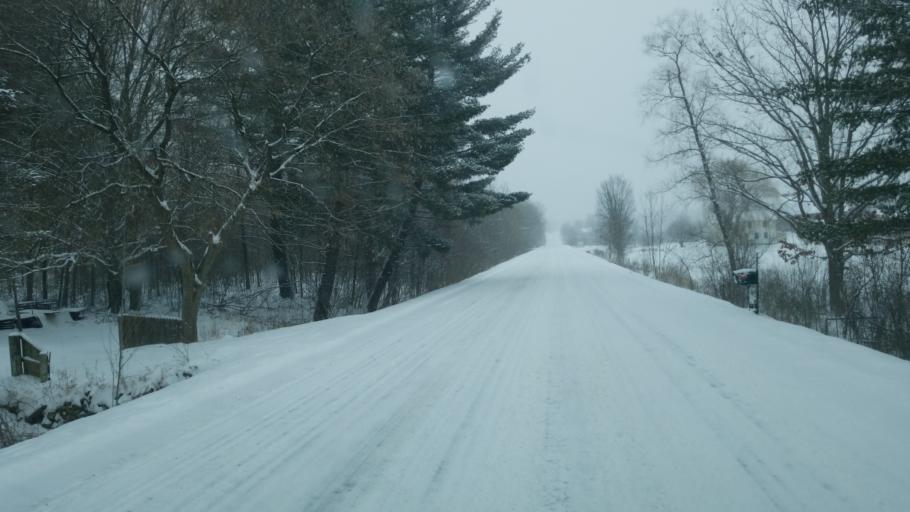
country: US
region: Michigan
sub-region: Mecosta County
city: Big Rapids
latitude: 43.5768
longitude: -85.4336
